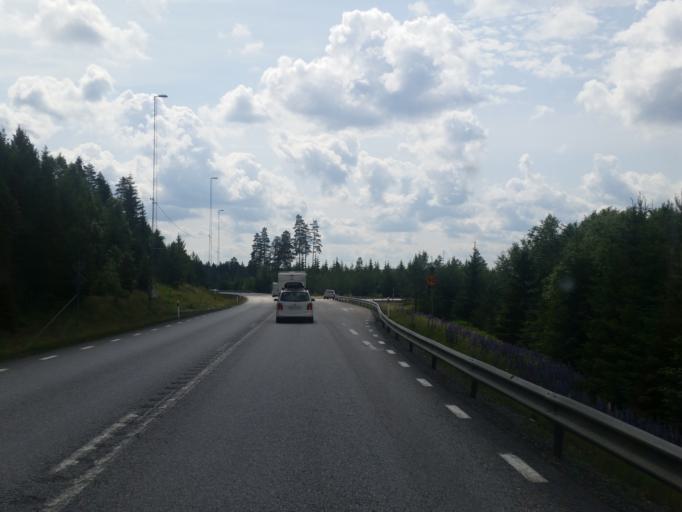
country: SE
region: OErebro
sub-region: Ljusnarsbergs Kommun
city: Kopparberg
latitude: 59.8957
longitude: 15.0177
